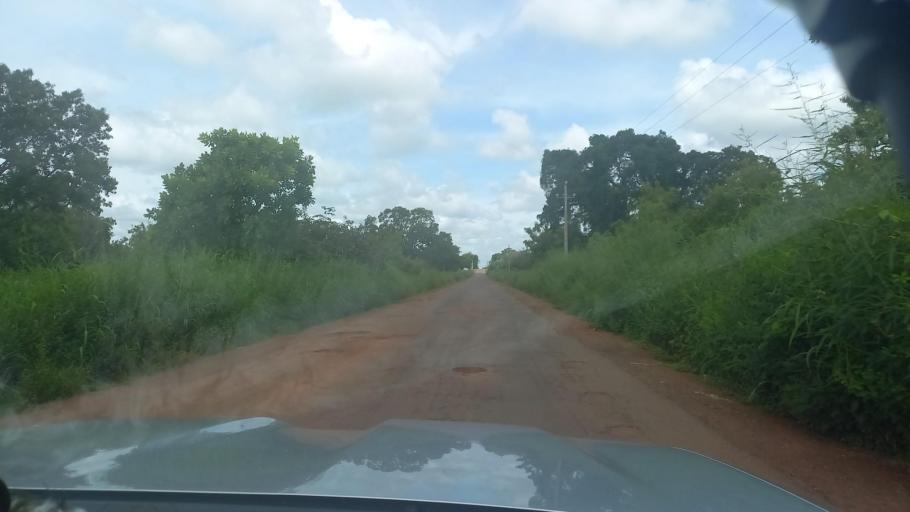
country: GM
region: Lower River
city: Kaiaf
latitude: 13.2159
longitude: -15.5437
